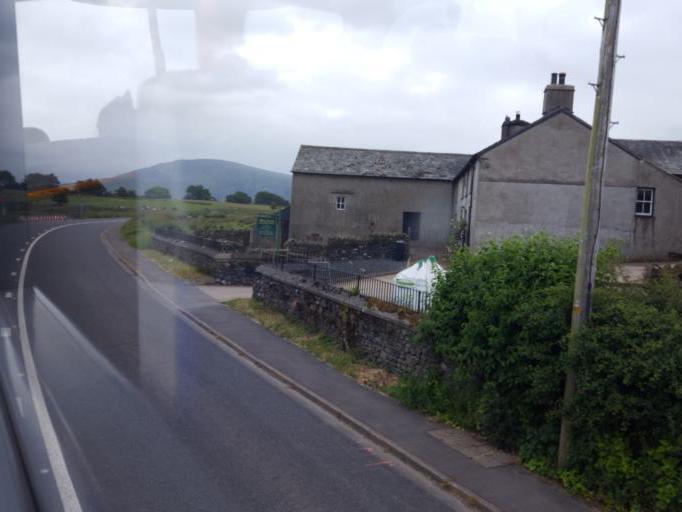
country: GB
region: England
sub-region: Cumbria
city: Keswick
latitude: 54.5968
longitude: -3.1118
